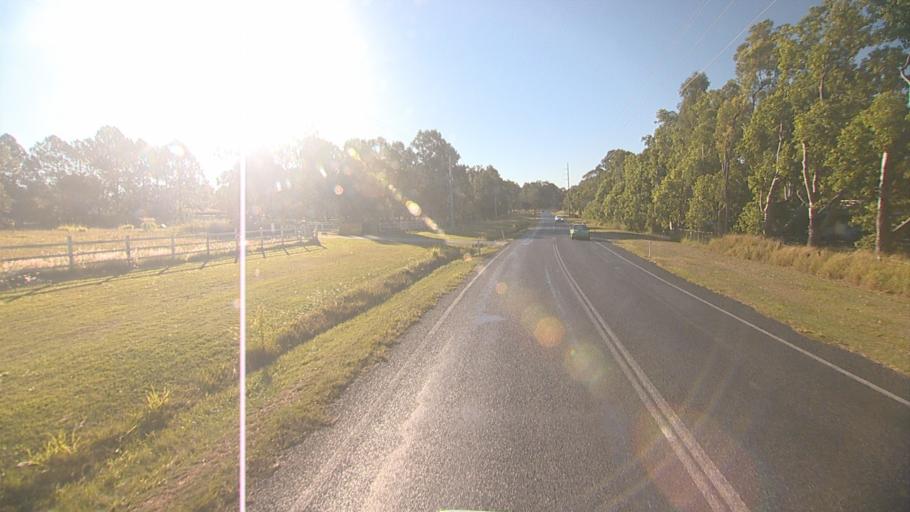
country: AU
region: Queensland
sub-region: Logan
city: Chambers Flat
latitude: -27.7437
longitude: 153.0880
